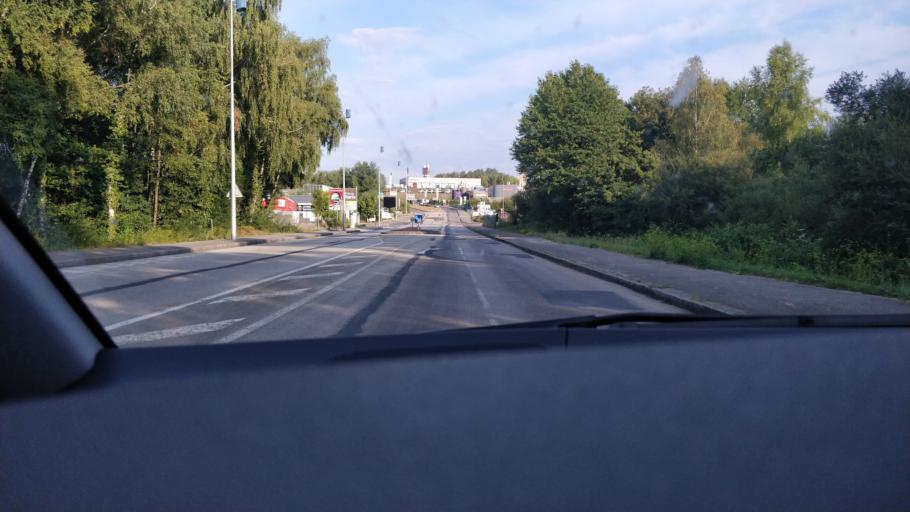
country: FR
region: Limousin
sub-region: Departement de la Haute-Vienne
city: Chaptelat
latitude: 45.8842
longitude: 1.2826
